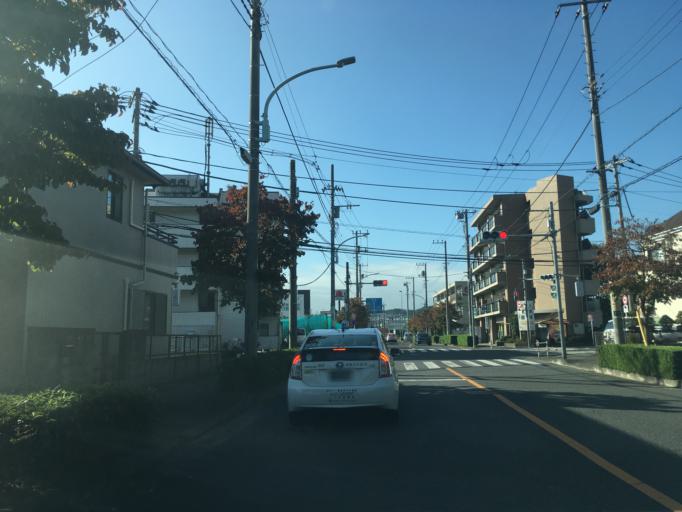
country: JP
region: Tokyo
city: Hino
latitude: 35.6714
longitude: 139.4091
